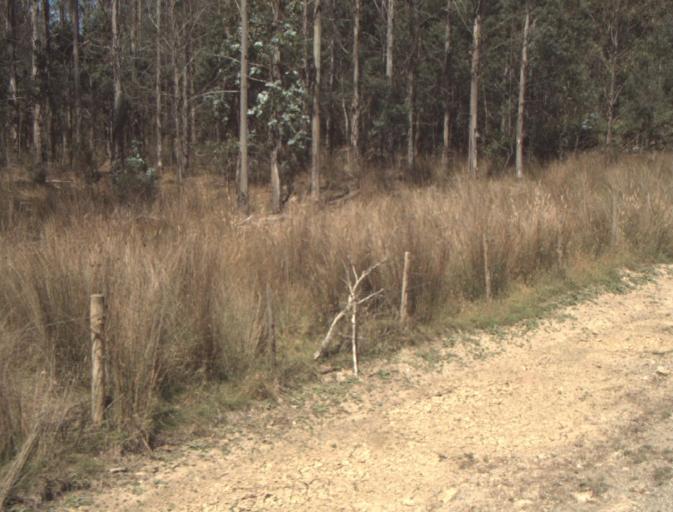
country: AU
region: Tasmania
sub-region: Dorset
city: Scottsdale
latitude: -41.3356
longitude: 147.4339
